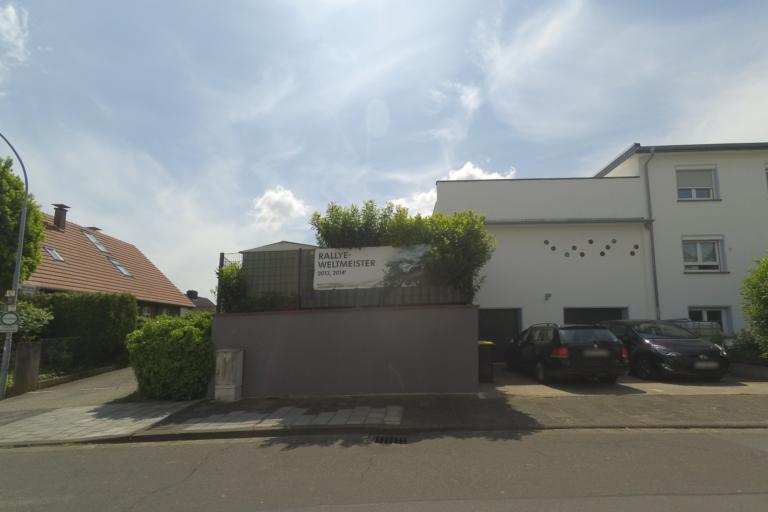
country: DE
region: Hesse
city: Nidderau
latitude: 50.2587
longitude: 8.9050
